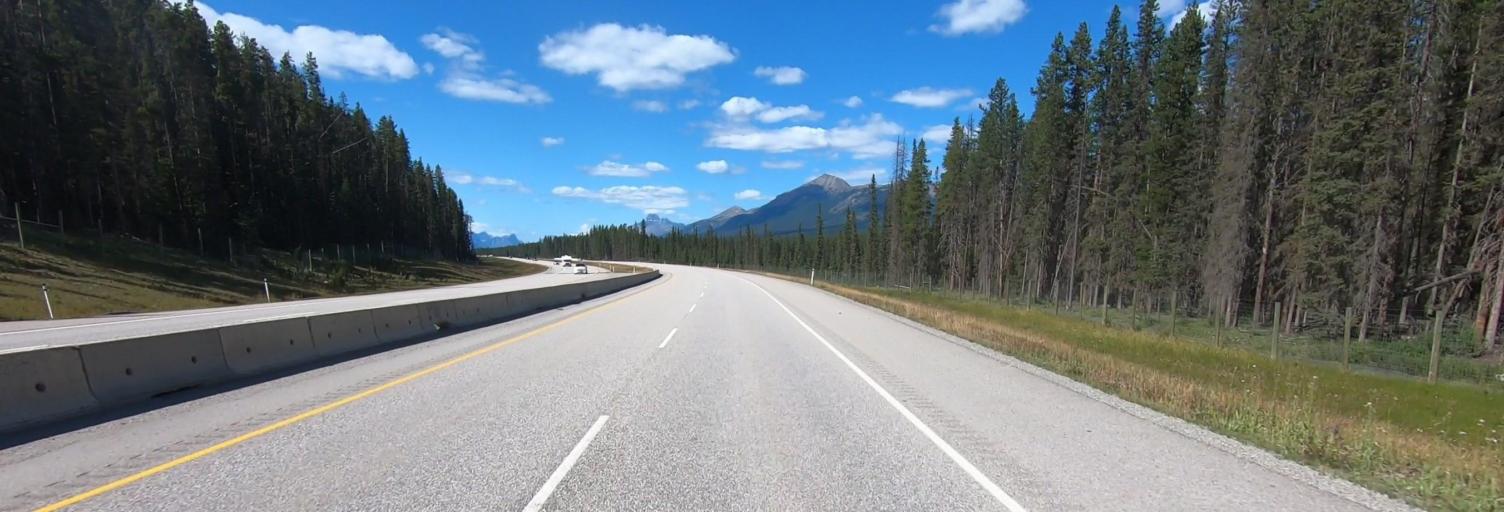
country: CA
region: Alberta
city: Lake Louise
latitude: 51.3315
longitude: -116.0548
